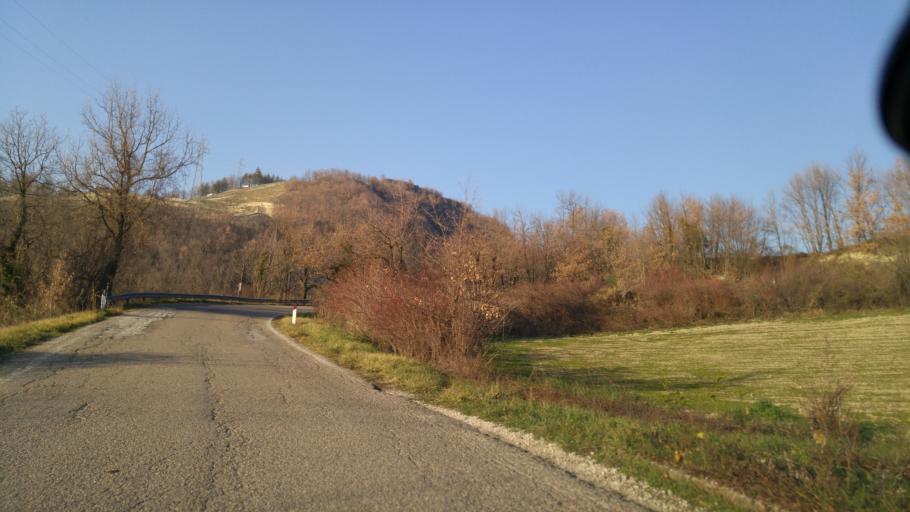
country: IT
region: The Marches
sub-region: Provincia di Pesaro e Urbino
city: Fermignano
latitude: 43.6604
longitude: 12.6646
